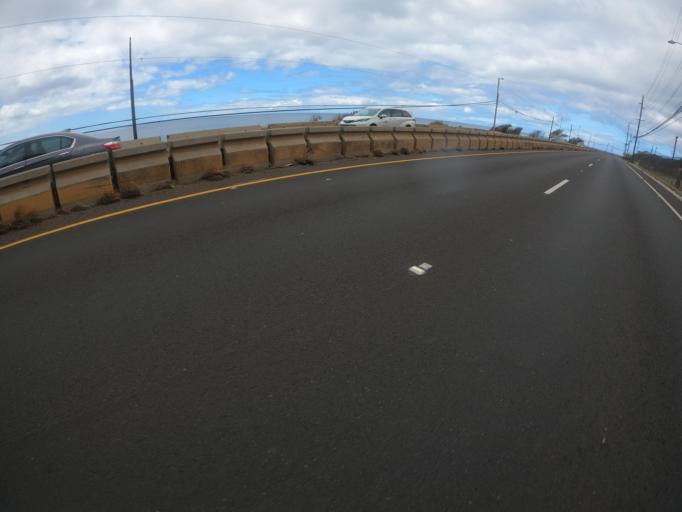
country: US
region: Hawaii
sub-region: Honolulu County
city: Ma'ili
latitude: 21.4003
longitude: -158.1741
